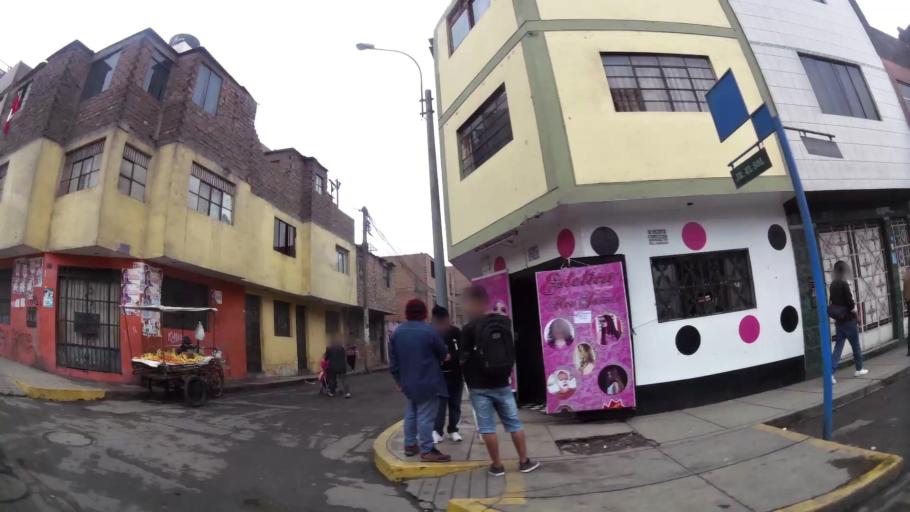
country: PE
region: Lima
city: Lima
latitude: -12.0508
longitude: -77.0025
